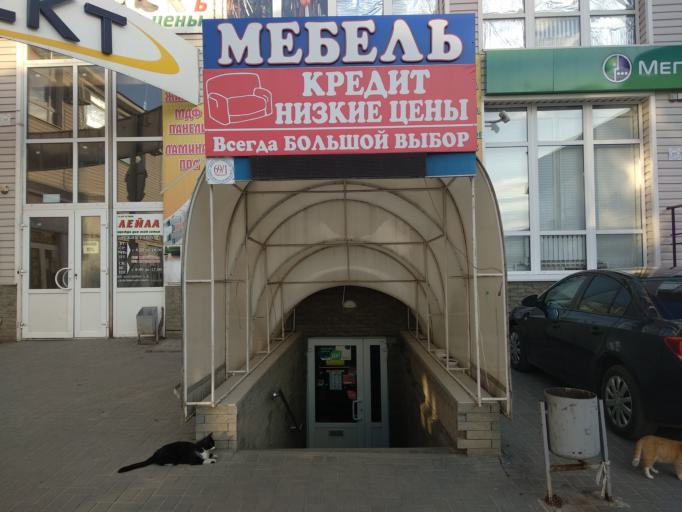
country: RU
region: Rostov
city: Millerovo
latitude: 48.9249
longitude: 40.4014
